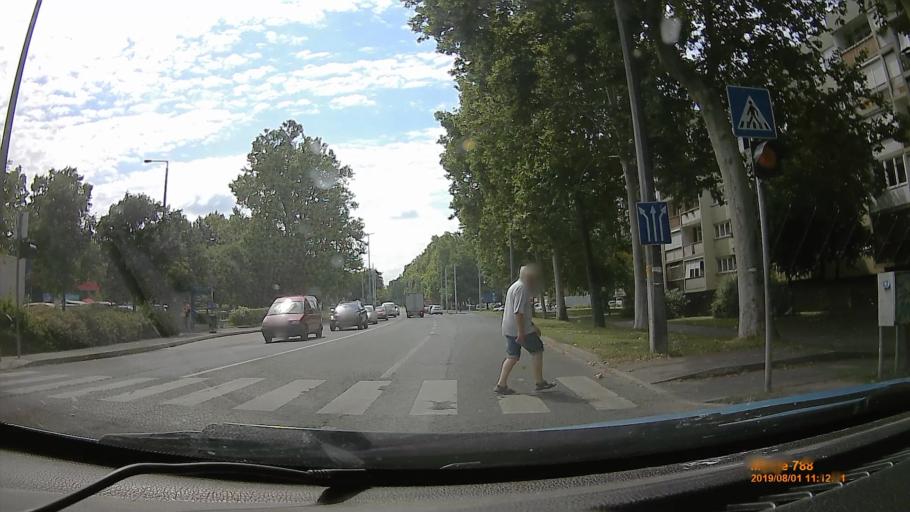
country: HU
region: Baranya
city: Pecs
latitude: 46.0435
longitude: 18.2155
